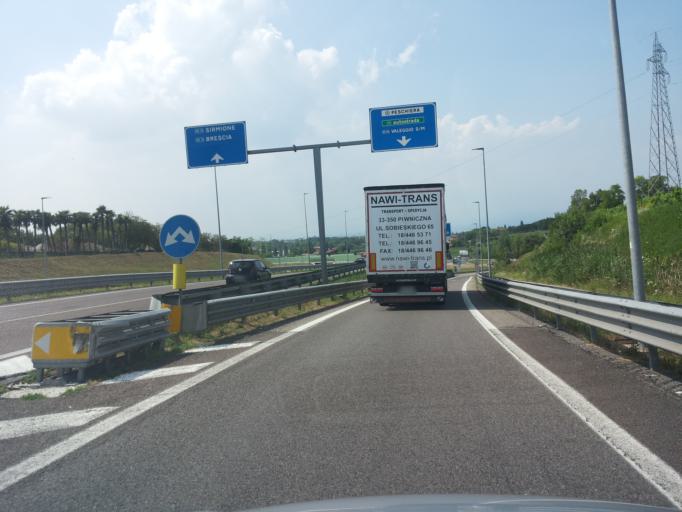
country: IT
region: Veneto
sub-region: Provincia di Verona
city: Cavalcaselle
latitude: 45.4303
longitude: 10.7095
